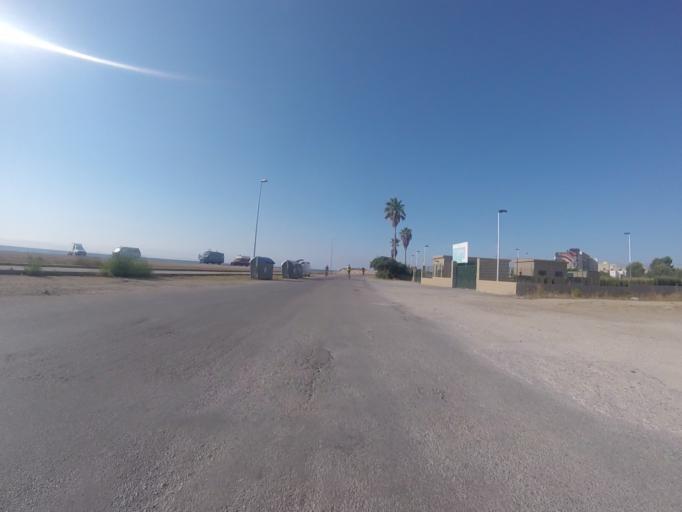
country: ES
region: Valencia
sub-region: Provincia de Castello
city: Benicarlo
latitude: 40.4185
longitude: 0.4361
